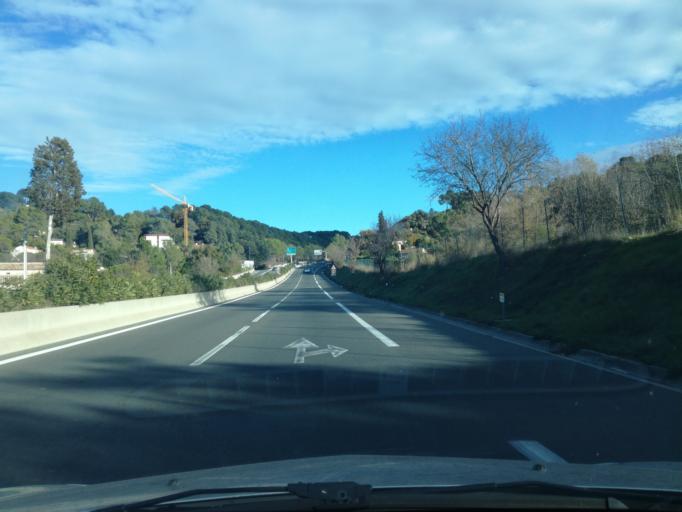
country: FR
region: Provence-Alpes-Cote d'Azur
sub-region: Departement des Alpes-Maritimes
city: Mouans-Sartoux
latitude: 43.6077
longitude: 6.9806
